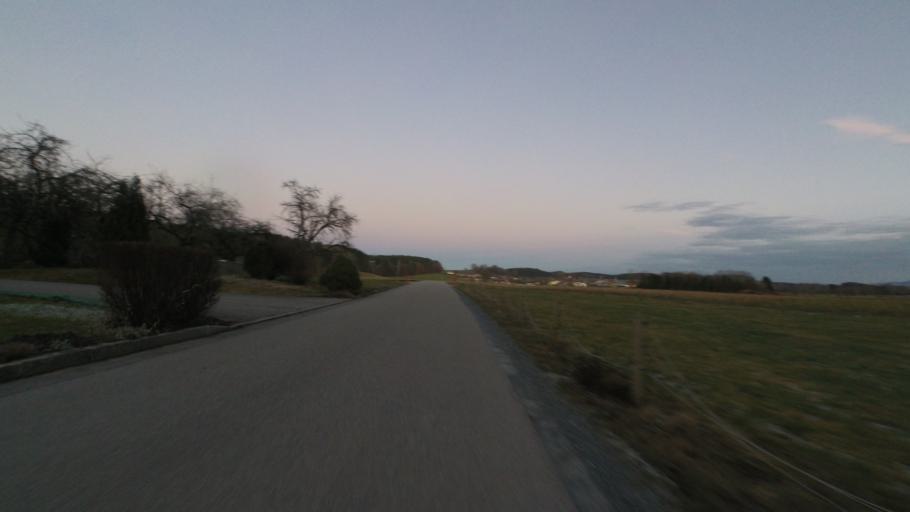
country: DE
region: Bavaria
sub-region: Upper Bavaria
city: Chieming
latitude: 47.9108
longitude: 12.5461
